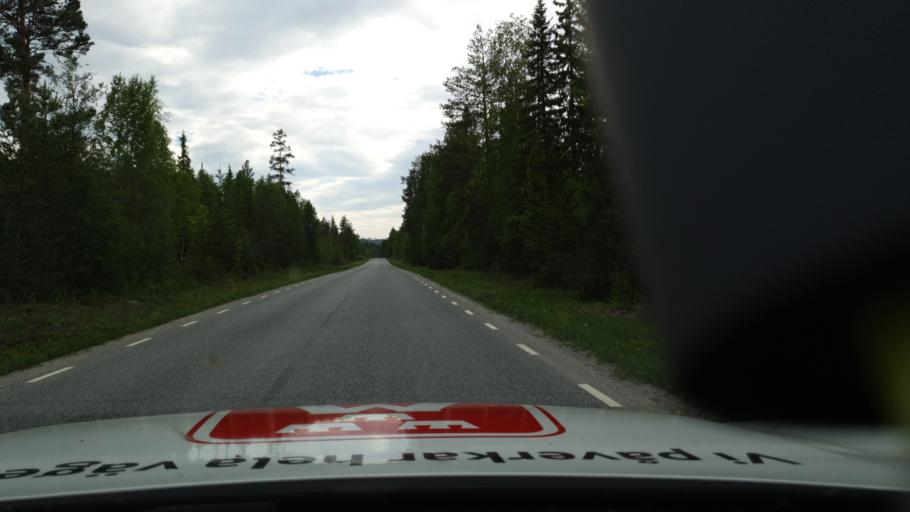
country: SE
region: Jaemtland
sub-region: Braecke Kommun
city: Braecke
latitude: 63.1568
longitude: 15.5584
